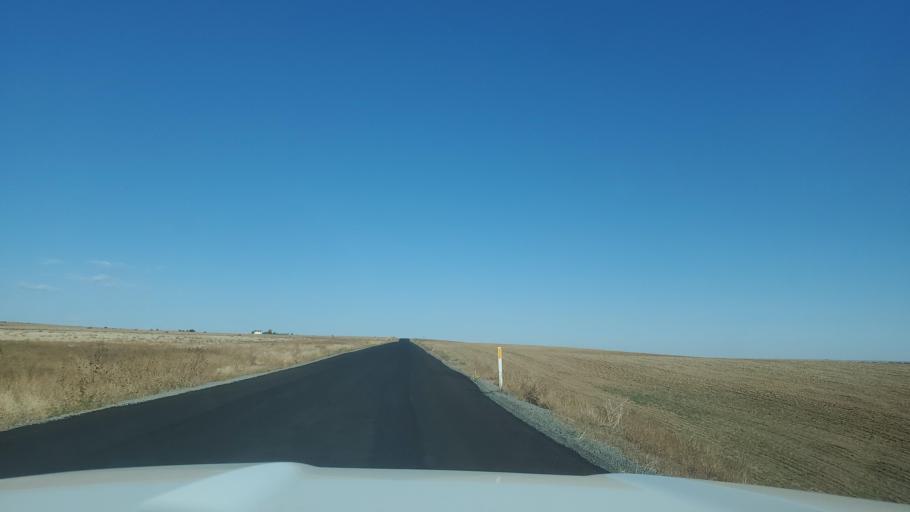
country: US
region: Colorado
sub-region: Adams County
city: Bennett
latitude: 39.7493
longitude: -104.3772
